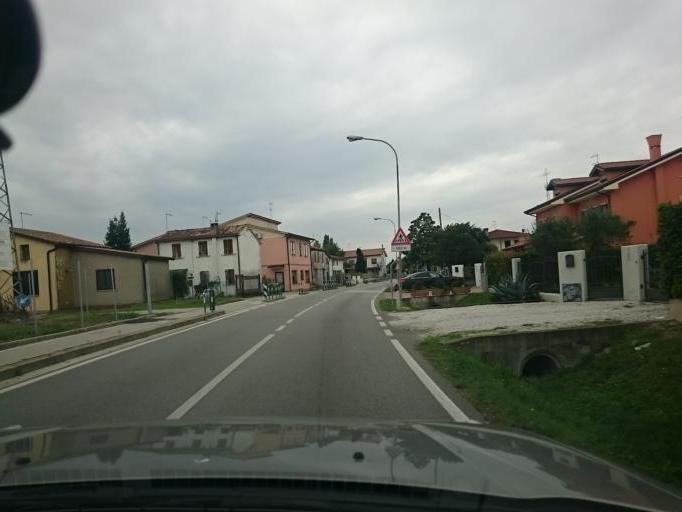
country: IT
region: Veneto
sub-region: Provincia di Padova
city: Piove di Sacco-Piovega
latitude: 45.2770
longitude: 12.0260
